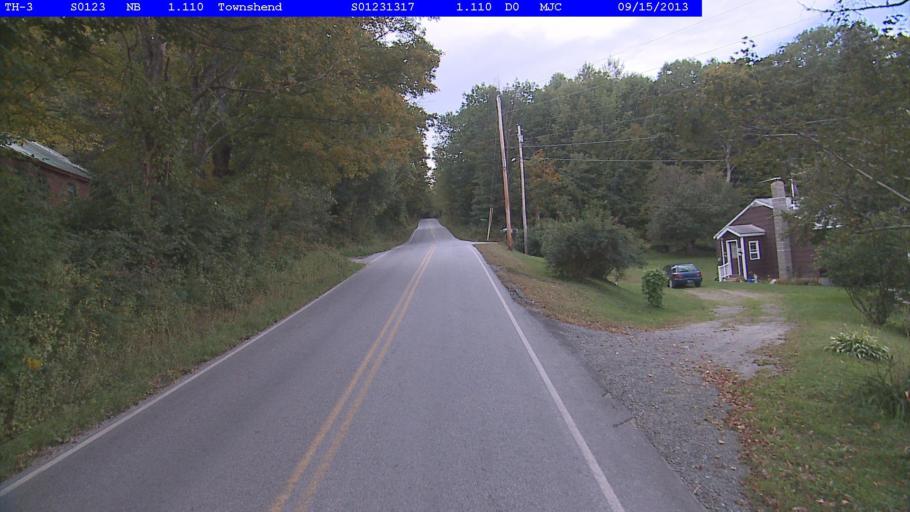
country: US
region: Vermont
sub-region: Windham County
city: Newfane
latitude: 43.0988
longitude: -72.7097
